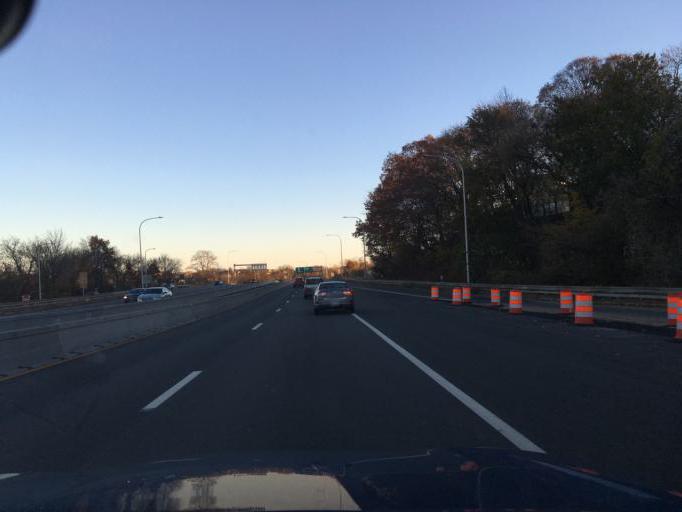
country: US
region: Rhode Island
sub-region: Providence County
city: Providence
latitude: 41.8165
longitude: -71.4477
